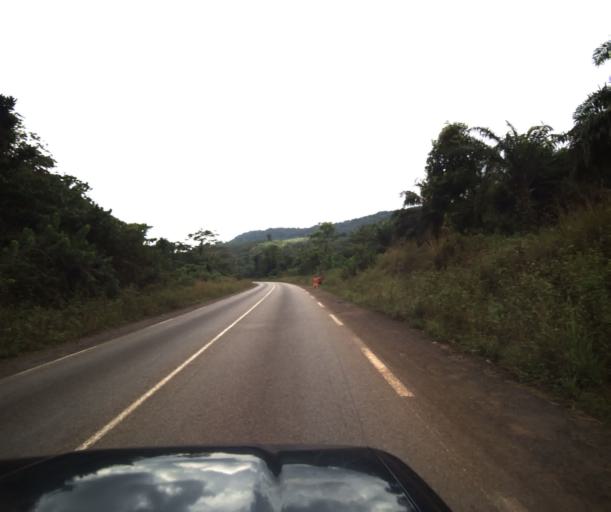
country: CM
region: Littoral
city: Edea
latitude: 3.8273
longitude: 10.3924
